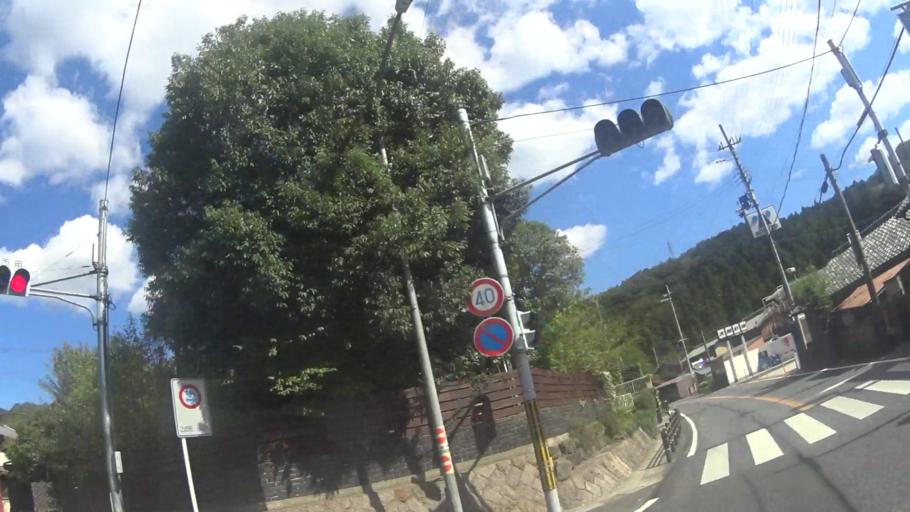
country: JP
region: Mie
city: Ueno-ebisumachi
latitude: 34.7715
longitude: 135.9950
